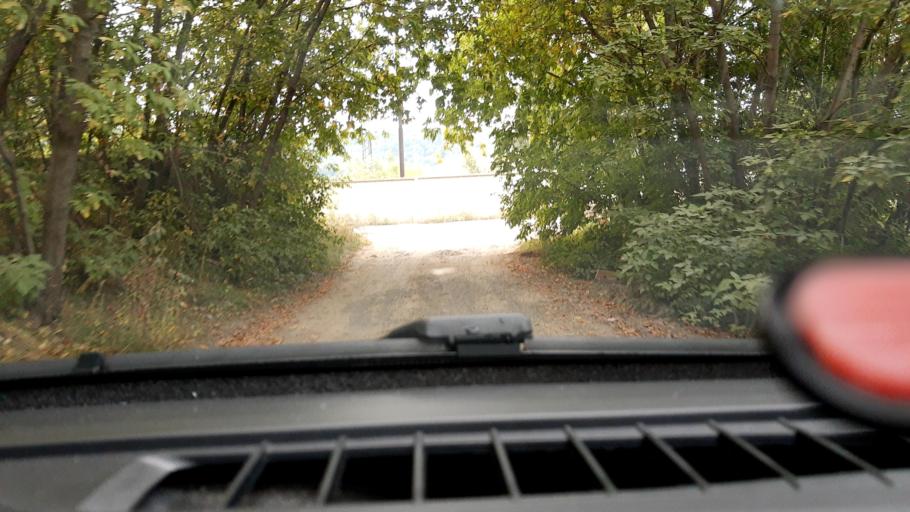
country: RU
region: Nizjnij Novgorod
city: Nizhniy Novgorod
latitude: 56.2360
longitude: 43.9150
